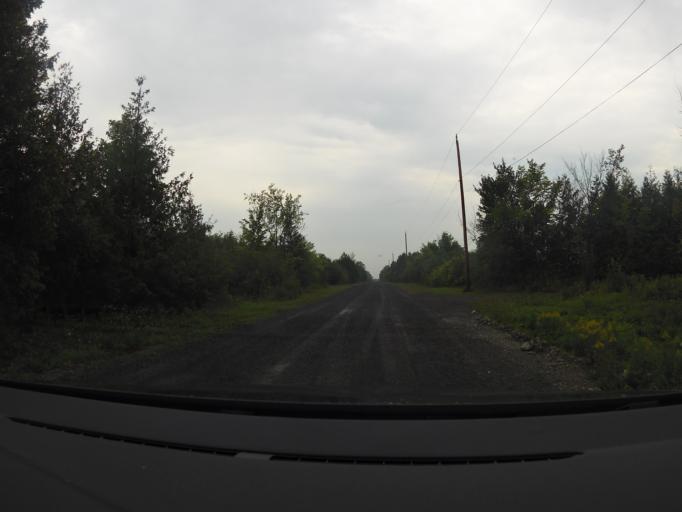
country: CA
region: Ontario
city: Carleton Place
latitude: 45.1911
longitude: -76.0583
